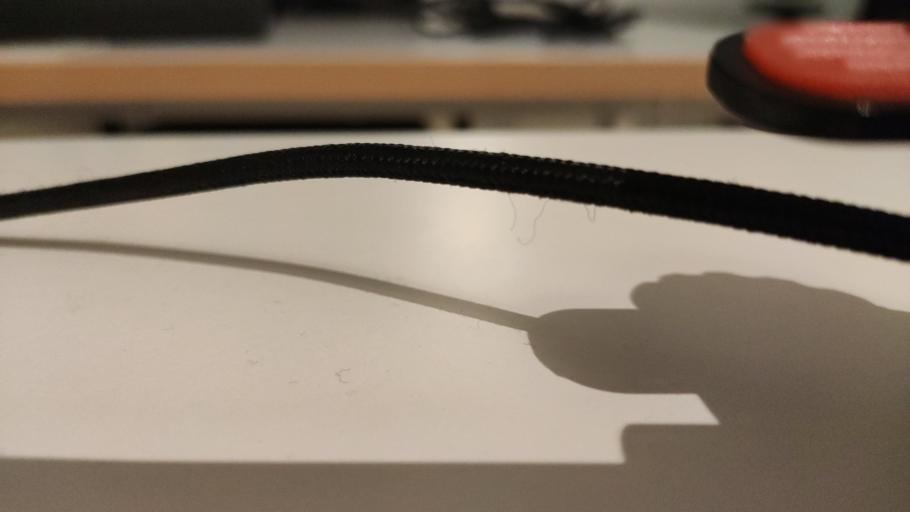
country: RU
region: Moskovskaya
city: Rogachevo
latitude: 56.4135
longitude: 37.2197
